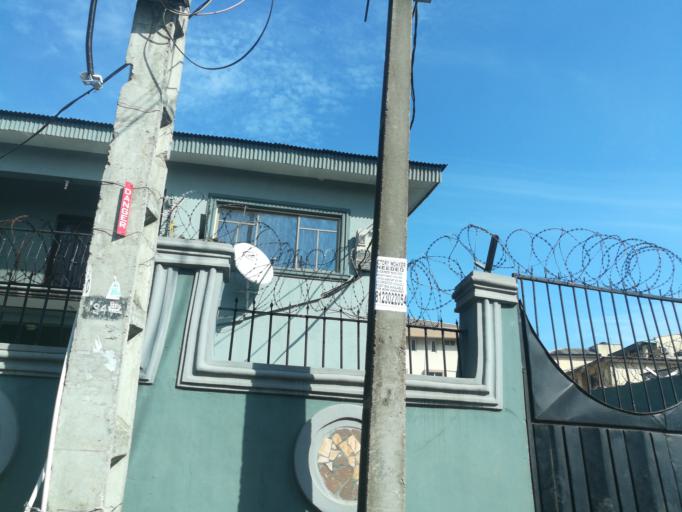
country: NG
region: Lagos
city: Ikeja
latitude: 6.5994
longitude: 3.3418
